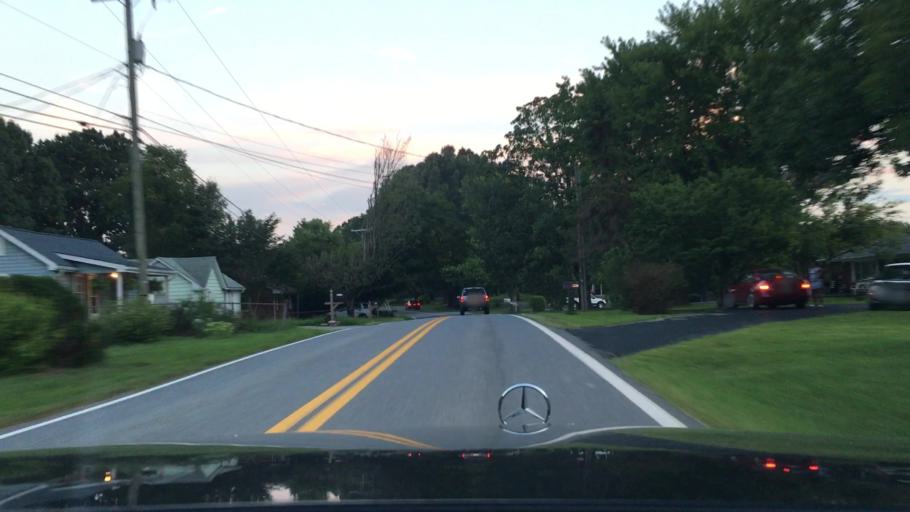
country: US
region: Virginia
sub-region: Campbell County
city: Altavista
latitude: 37.1448
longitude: -79.2959
